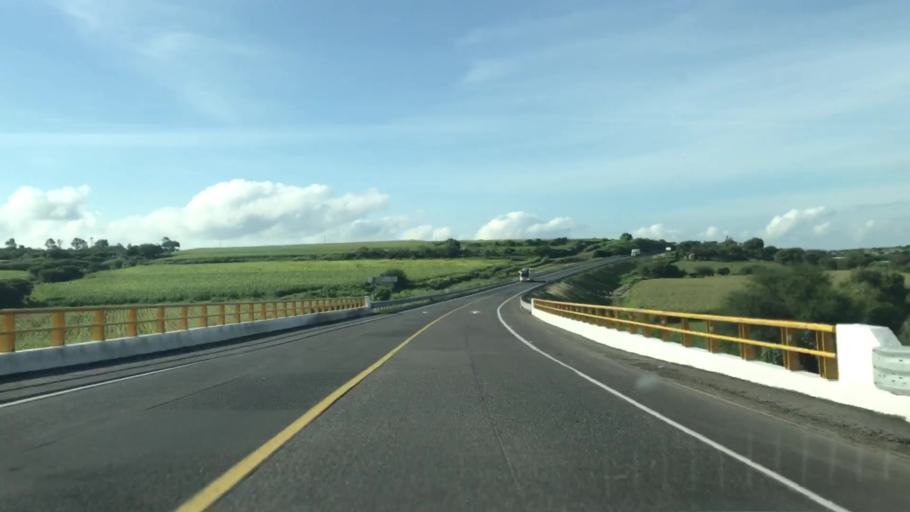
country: MX
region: Jalisco
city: Encarnacion de Diaz
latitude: 21.4182
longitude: -102.2053
